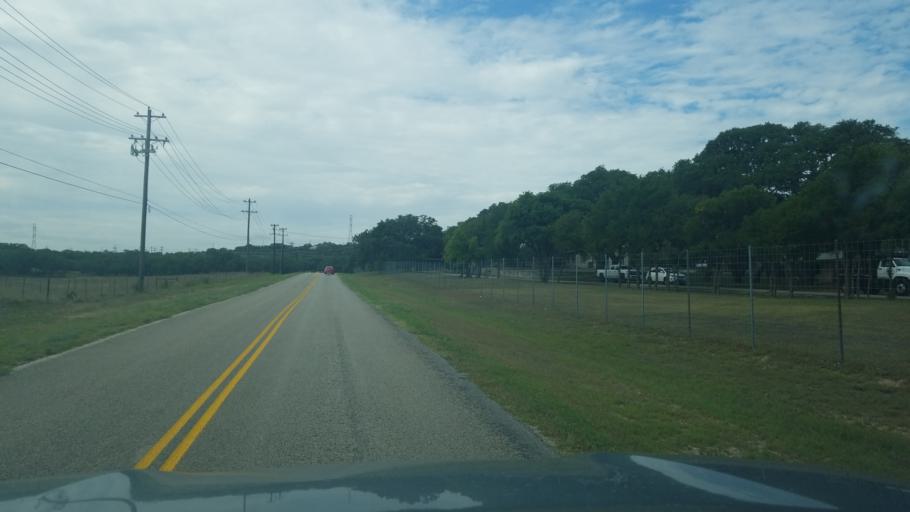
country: US
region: Texas
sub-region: Comal County
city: Bulverde
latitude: 29.7851
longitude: -98.4134
